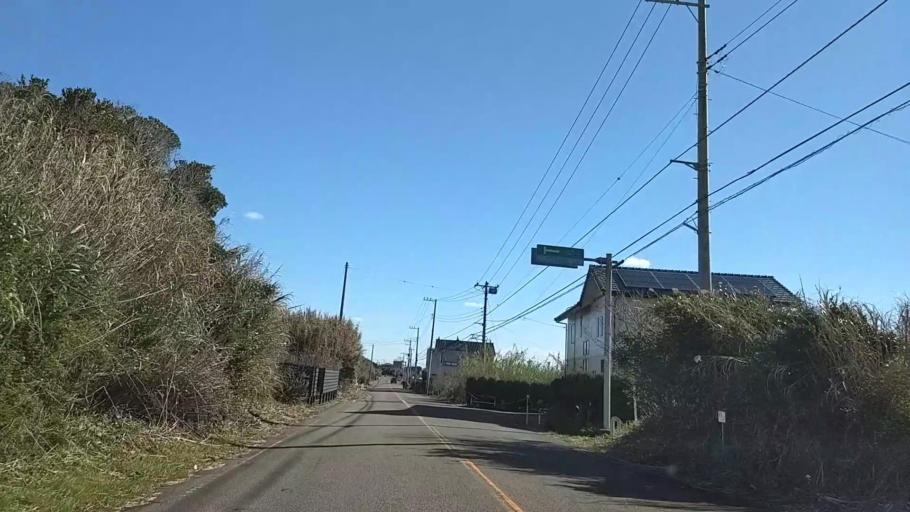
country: JP
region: Chiba
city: Tateyama
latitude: 34.9084
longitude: 139.8326
